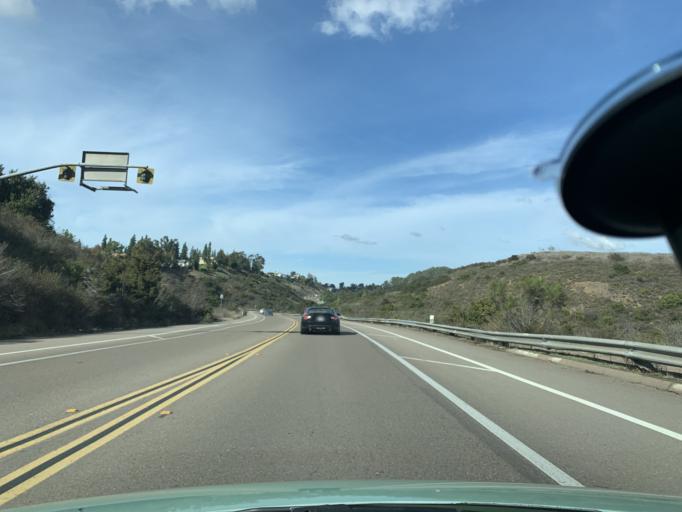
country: US
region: California
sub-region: San Diego County
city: San Diego
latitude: 32.7988
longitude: -117.1720
